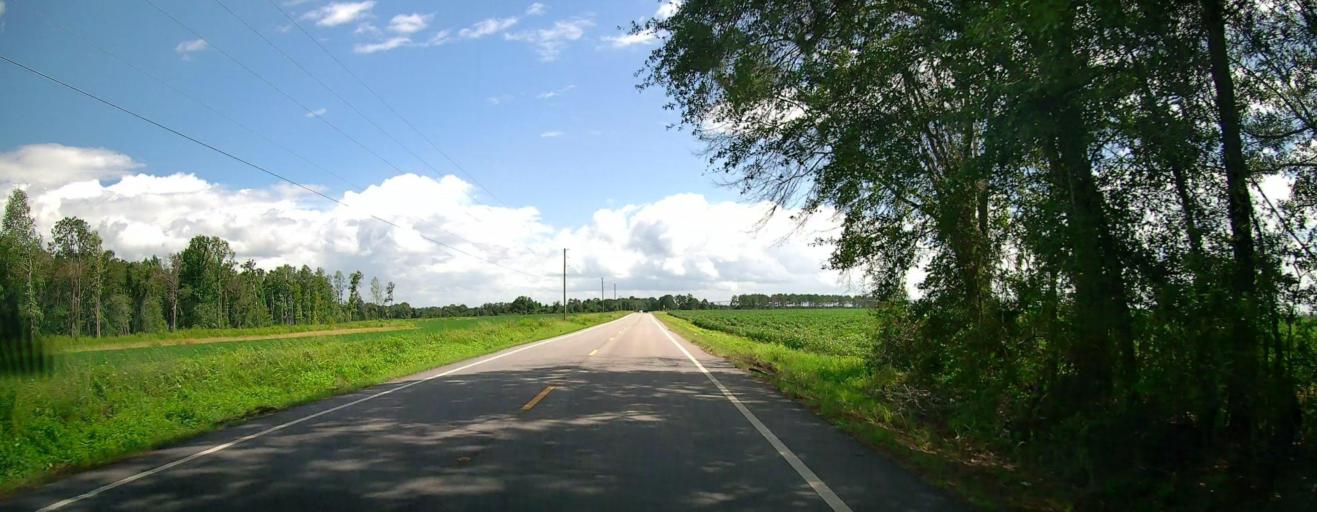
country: US
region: Georgia
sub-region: Irwin County
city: Ocilla
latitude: 31.6513
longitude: -83.1738
